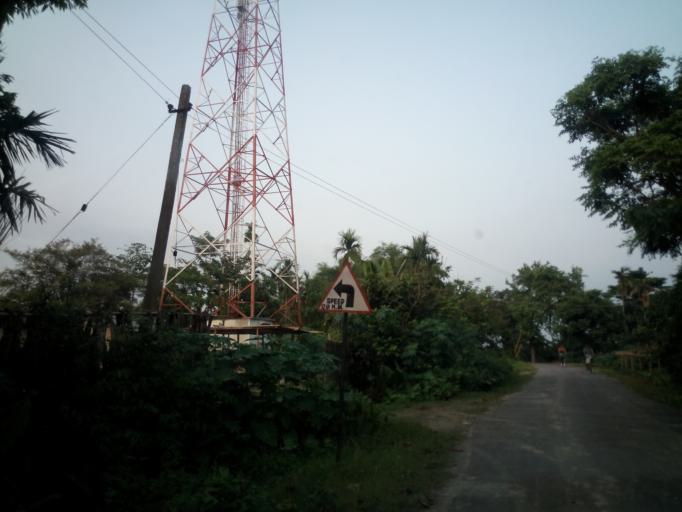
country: IN
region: Assam
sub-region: Udalguri
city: Udalguri
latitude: 26.6835
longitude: 92.1124
